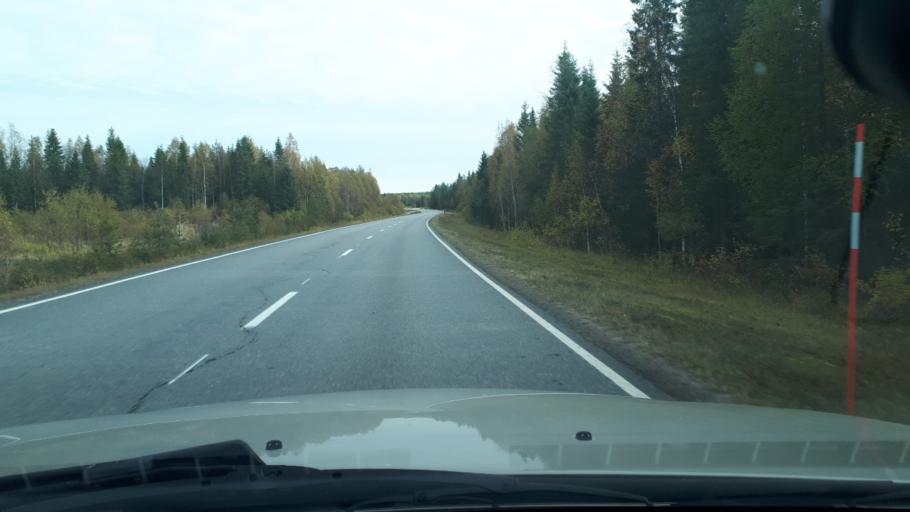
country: FI
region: Lapland
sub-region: Rovaniemi
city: Ranua
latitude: 65.9835
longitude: 26.1525
